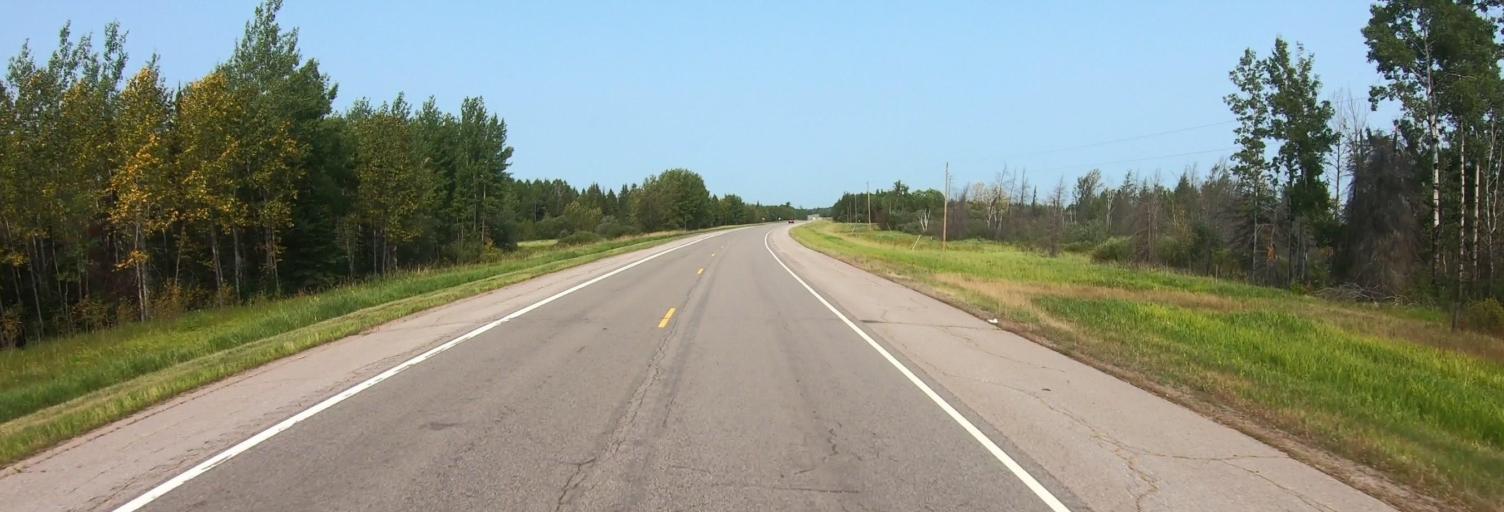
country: US
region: Minnesota
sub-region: Saint Louis County
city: Mountain Iron
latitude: 47.8765
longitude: -92.7586
